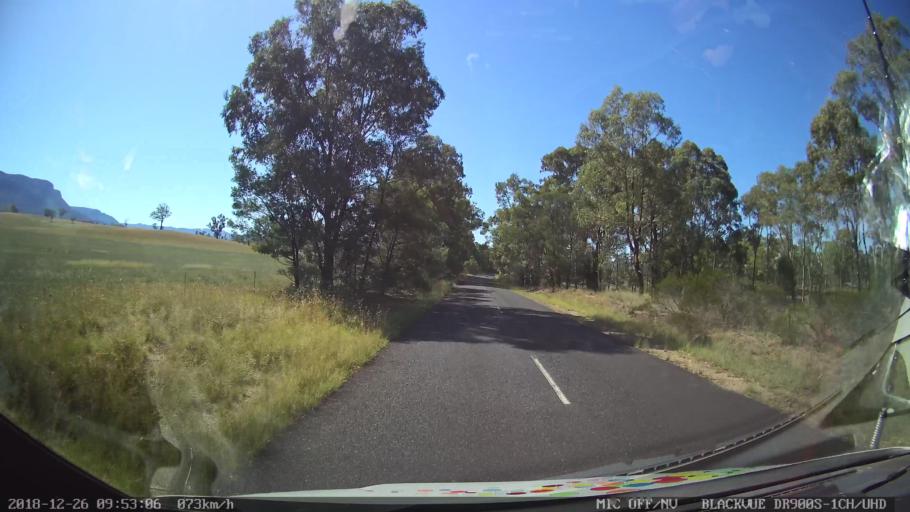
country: AU
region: New South Wales
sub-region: Mid-Western Regional
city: Kandos
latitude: -33.0174
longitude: 150.1519
